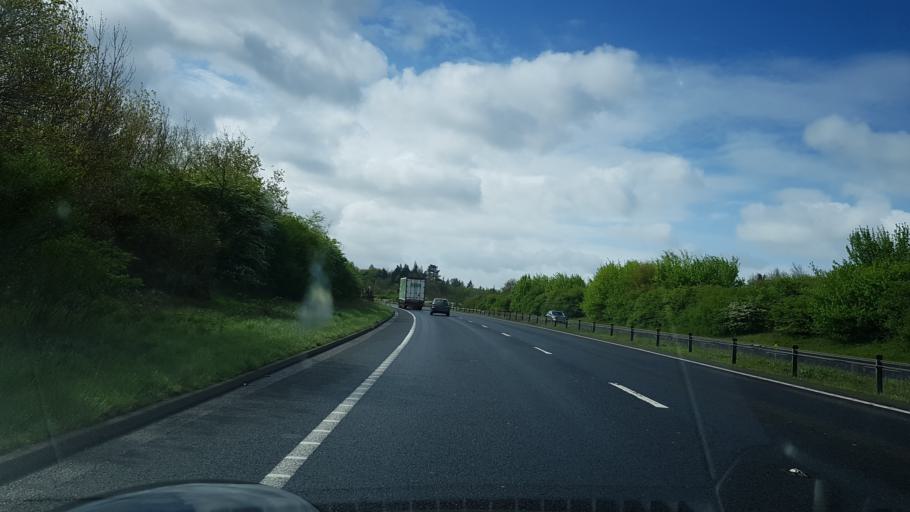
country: GB
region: England
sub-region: Hampshire
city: Highclere
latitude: 51.3711
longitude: -1.3646
